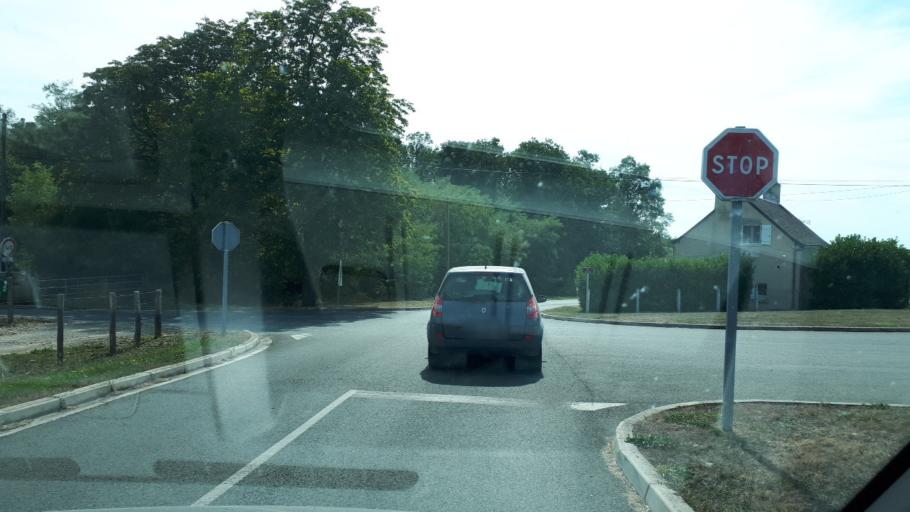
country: FR
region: Centre
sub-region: Departement du Loir-et-Cher
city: Montoire-sur-le-Loir
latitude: 47.7284
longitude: 0.8334
